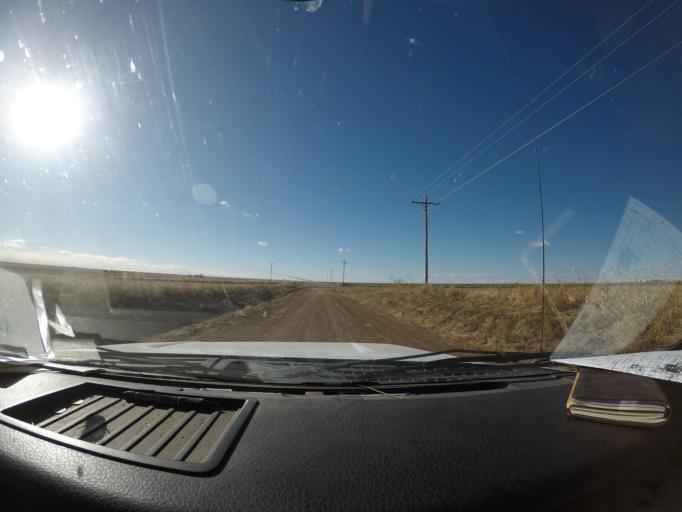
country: US
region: New Mexico
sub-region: Curry County
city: Clovis
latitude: 34.5650
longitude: -103.2656
